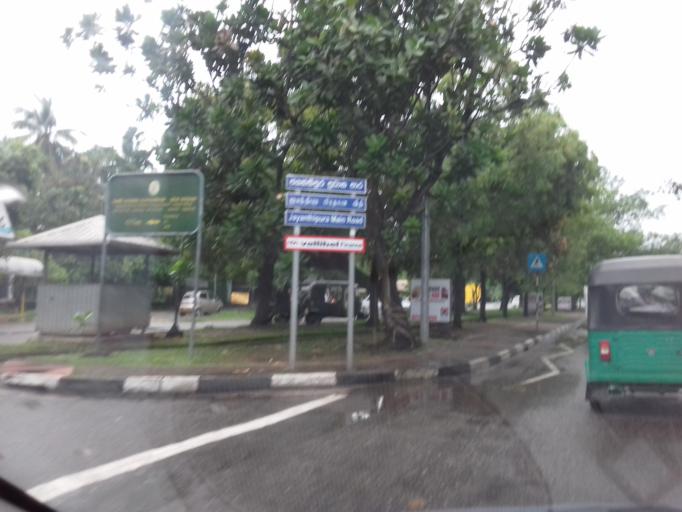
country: LK
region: Western
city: Battaramulla South
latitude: 6.8940
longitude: 79.9160
